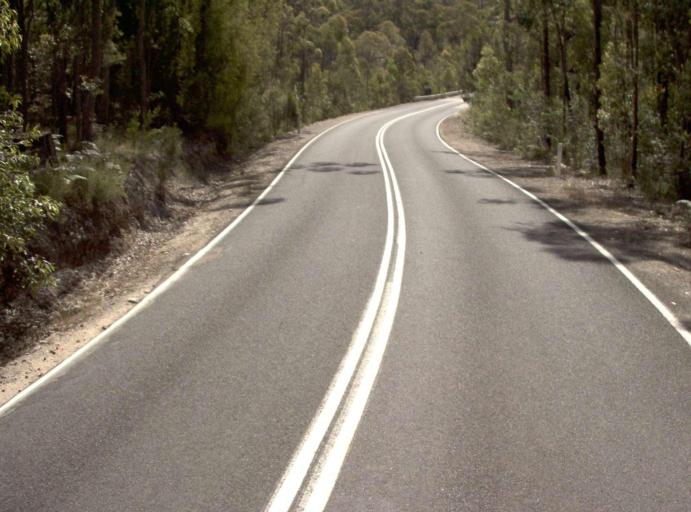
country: AU
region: New South Wales
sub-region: Bega Valley
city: Eden
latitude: -37.5034
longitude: 149.6857
